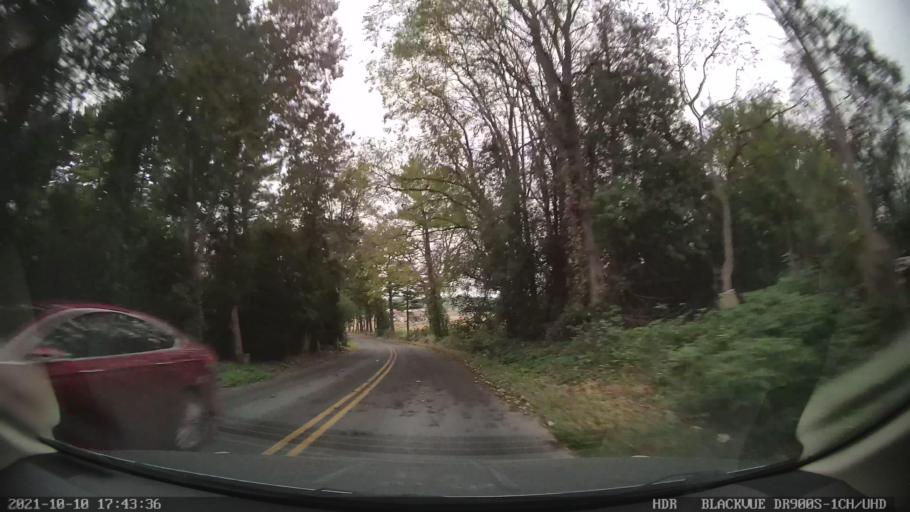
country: US
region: Pennsylvania
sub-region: Berks County
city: Topton
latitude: 40.5386
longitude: -75.6769
